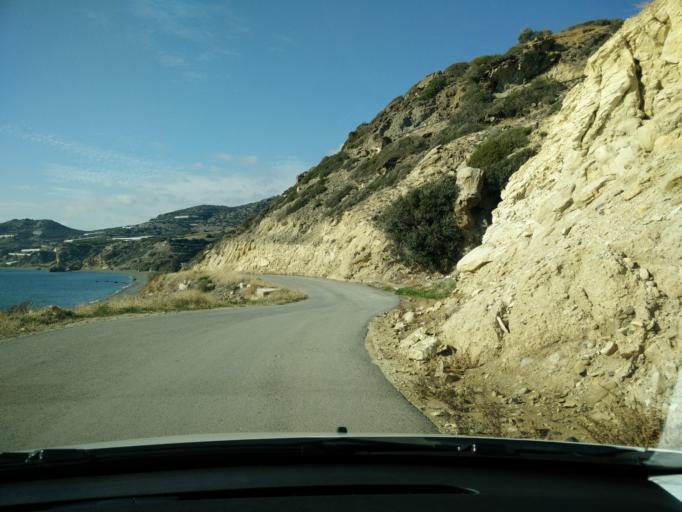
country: GR
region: Crete
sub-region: Nomos Lasithiou
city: Gra Liyia
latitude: 34.9894
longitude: 25.5408
